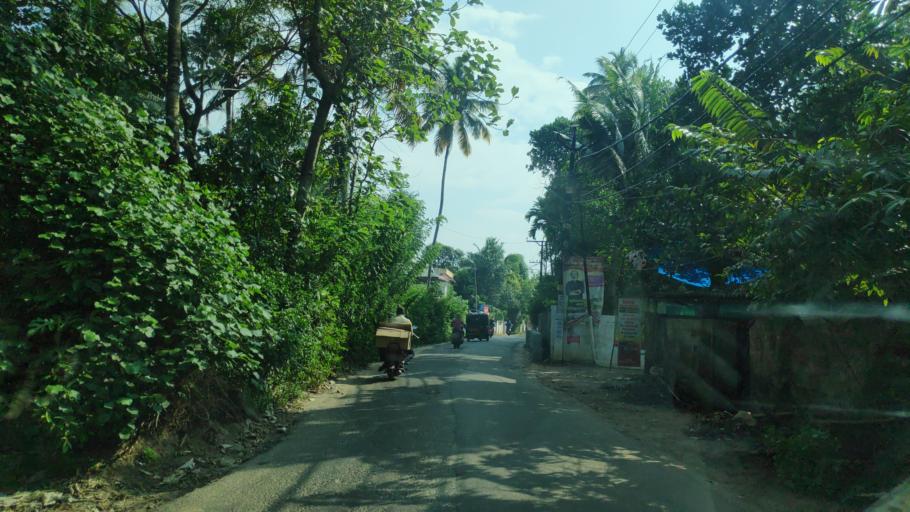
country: IN
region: Kerala
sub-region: Alappuzha
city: Alleppey
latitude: 9.5086
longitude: 76.3203
